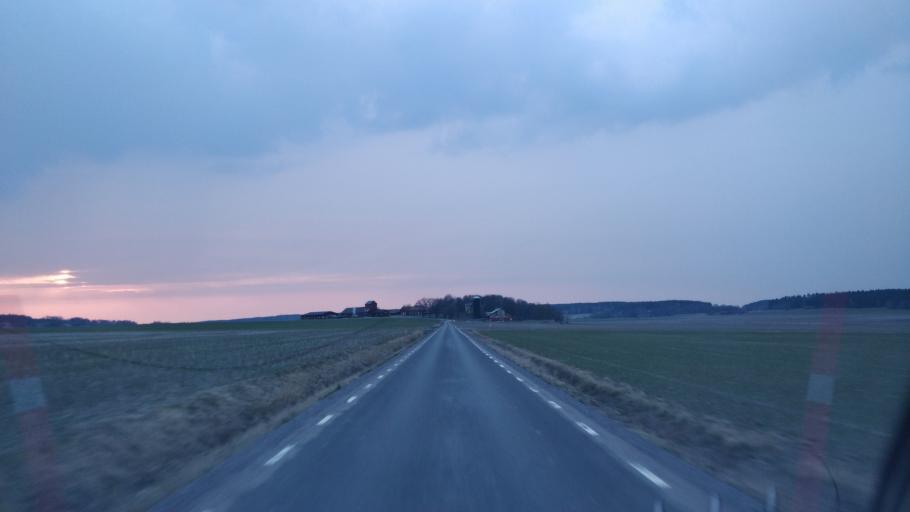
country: SE
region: Uppsala
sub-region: Enkopings Kommun
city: Orsundsbro
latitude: 59.7356
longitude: 17.1916
